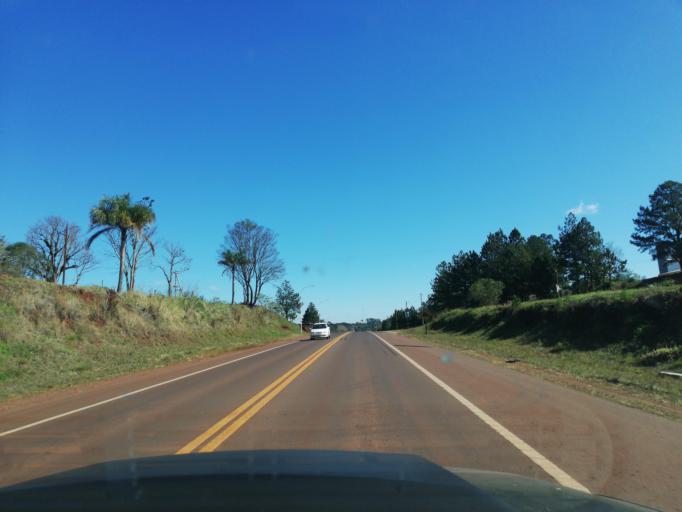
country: AR
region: Misiones
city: Aristobulo del Valle
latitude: -27.0948
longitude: -54.8700
